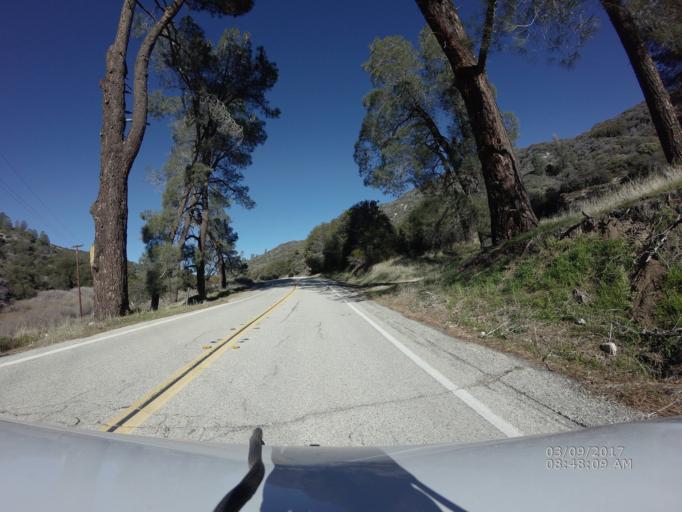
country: US
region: California
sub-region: Los Angeles County
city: Green Valley
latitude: 34.7007
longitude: -118.5172
